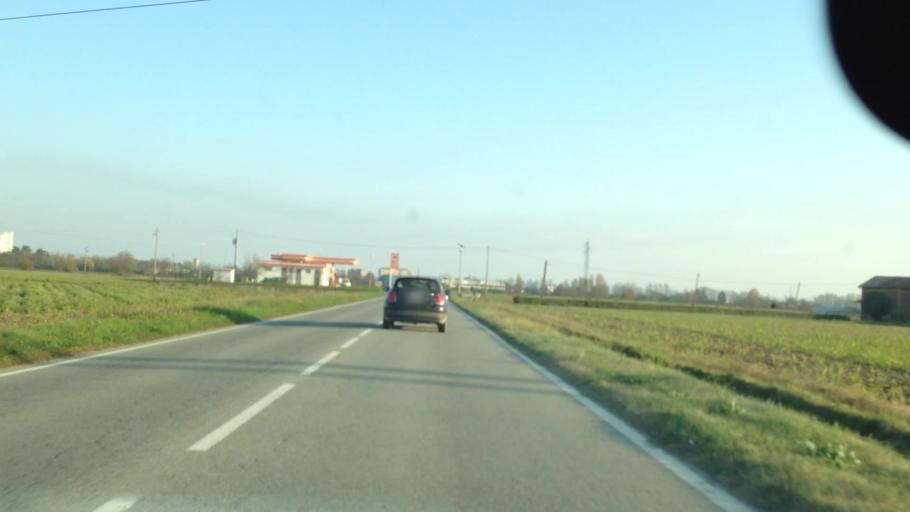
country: IT
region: Piedmont
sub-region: Provincia di Vercelli
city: Livorno Ferraris
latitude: 45.2916
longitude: 8.0535
